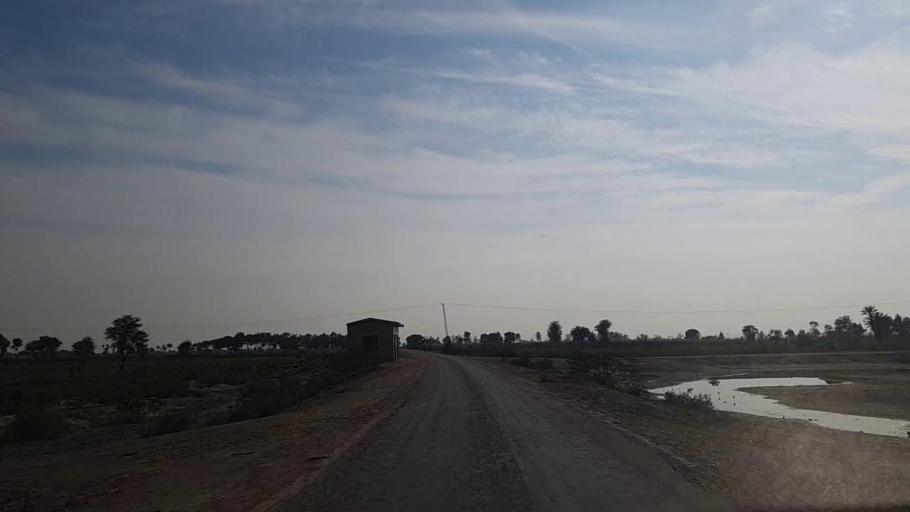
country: PK
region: Sindh
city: Daur
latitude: 26.4668
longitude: 68.4176
